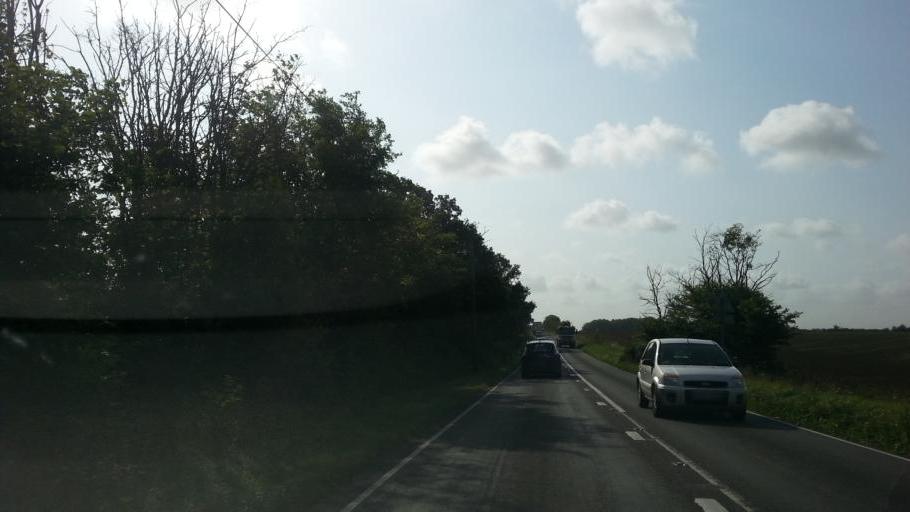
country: GB
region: England
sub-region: Cambridgeshire
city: Papworth Everard
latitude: 52.2353
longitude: -0.1077
